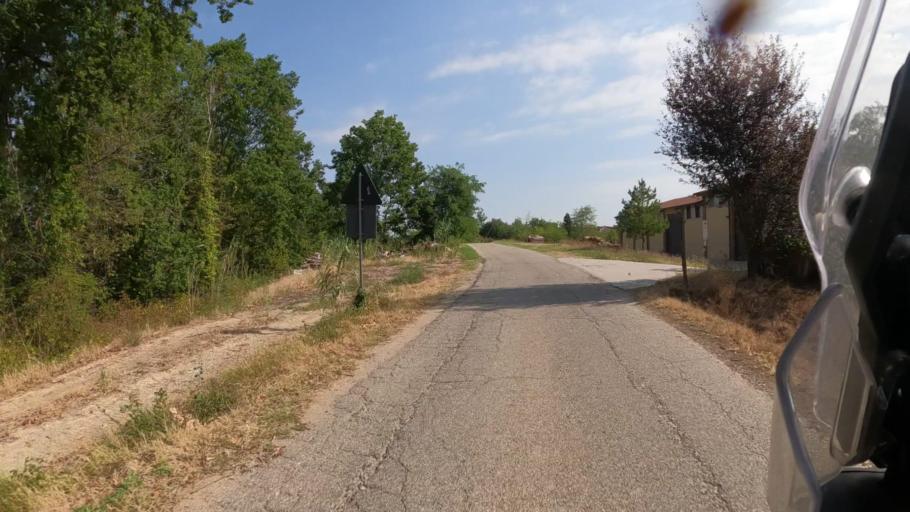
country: IT
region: Piedmont
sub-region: Provincia di Asti
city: Viarigi
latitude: 44.9642
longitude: 8.3820
